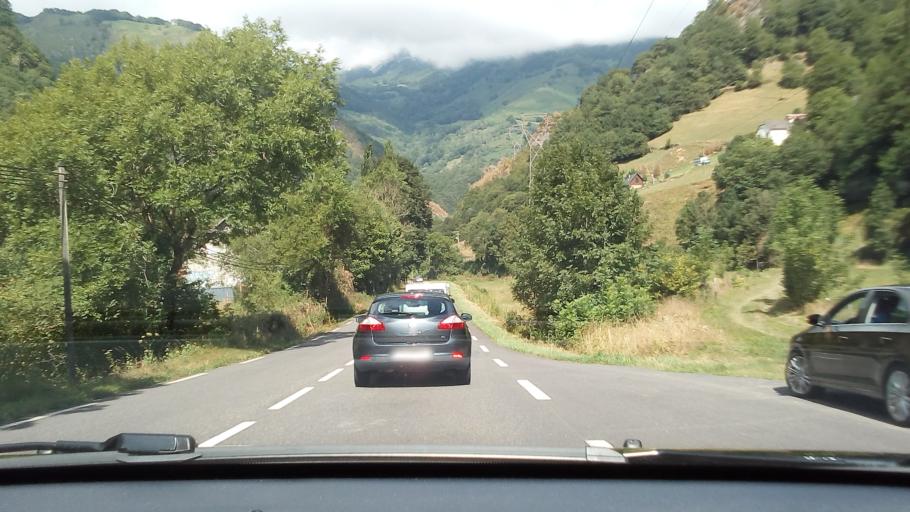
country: FR
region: Aquitaine
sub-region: Departement des Pyrenees-Atlantiques
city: Laruns
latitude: 42.9405
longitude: -0.6020
